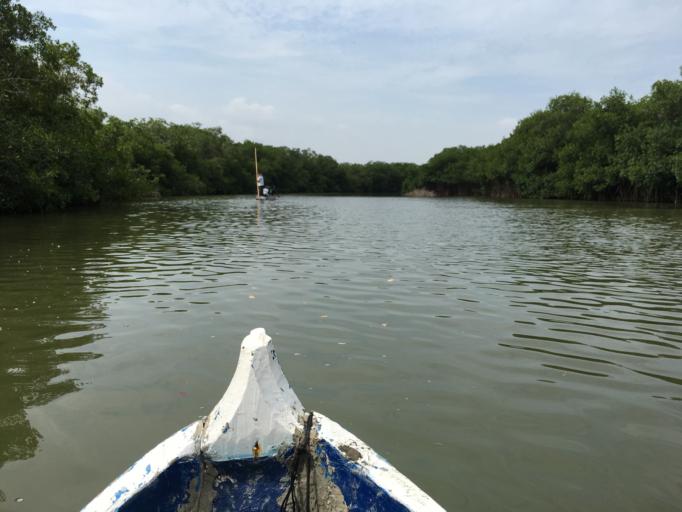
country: CO
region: Bolivar
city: Cartagena
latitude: 10.4919
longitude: -75.4869
